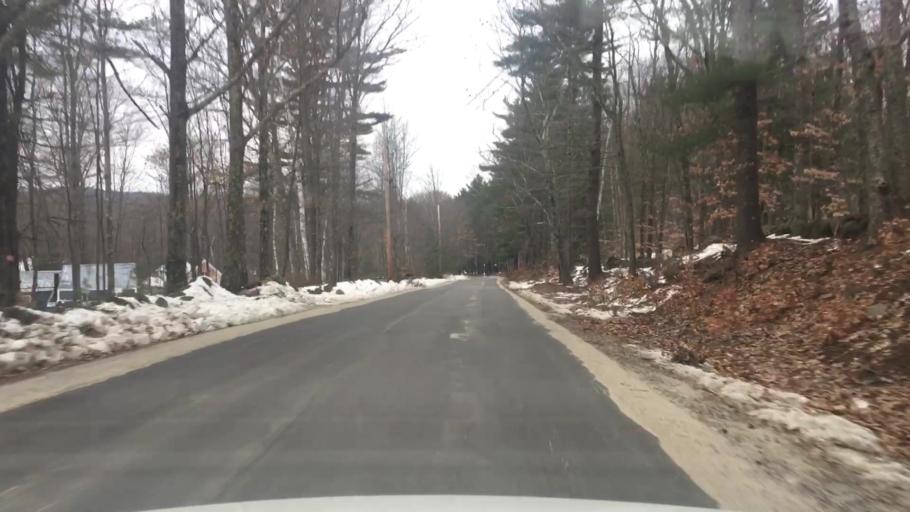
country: US
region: New Hampshire
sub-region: Merrimack County
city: Hopkinton
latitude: 43.1772
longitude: -71.6750
